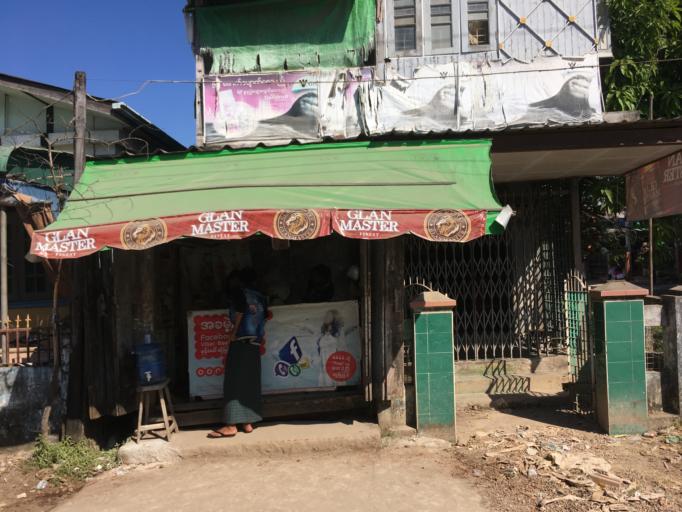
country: MM
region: Mon
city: Mawlamyine
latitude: 16.4963
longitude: 97.6353
